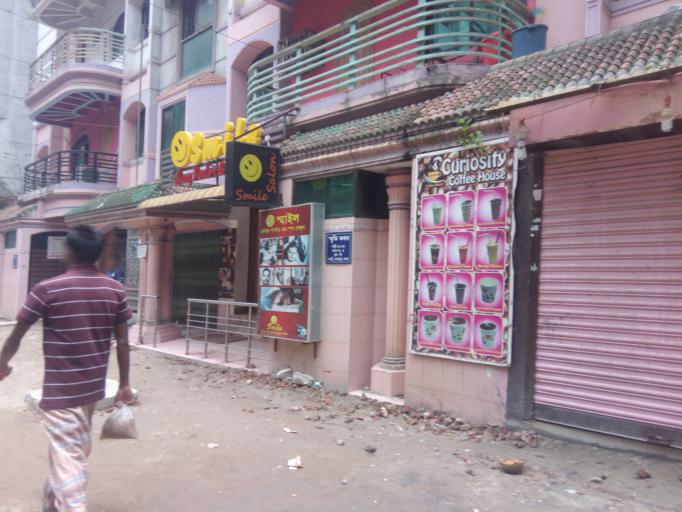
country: BD
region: Dhaka
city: Paltan
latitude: 23.7624
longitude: 90.4288
